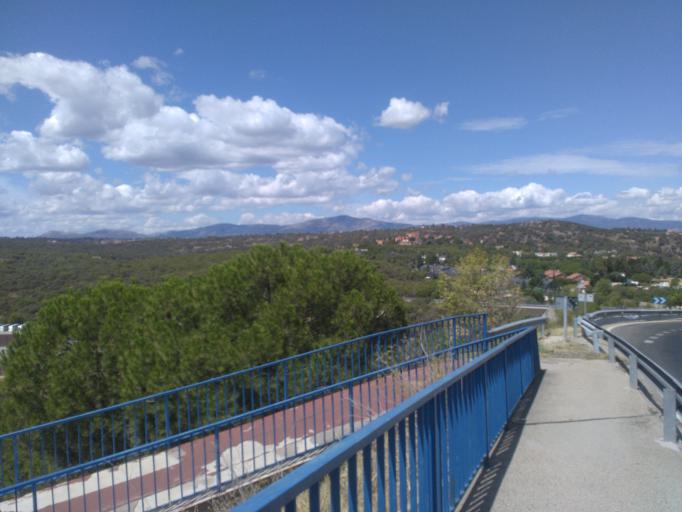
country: ES
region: Madrid
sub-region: Provincia de Madrid
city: Torrelodones
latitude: 40.5814
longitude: -3.9623
